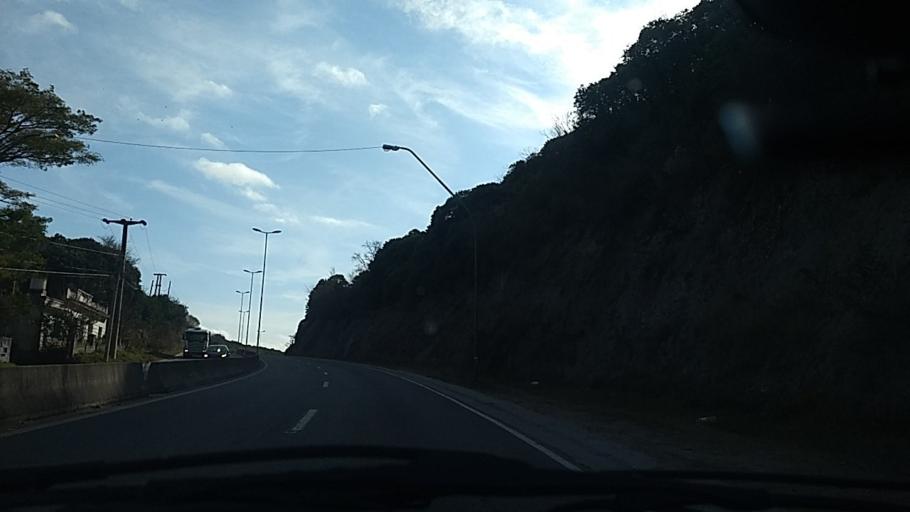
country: AR
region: Cordoba
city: Rio Ceballos
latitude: -31.1599
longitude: -64.3008
